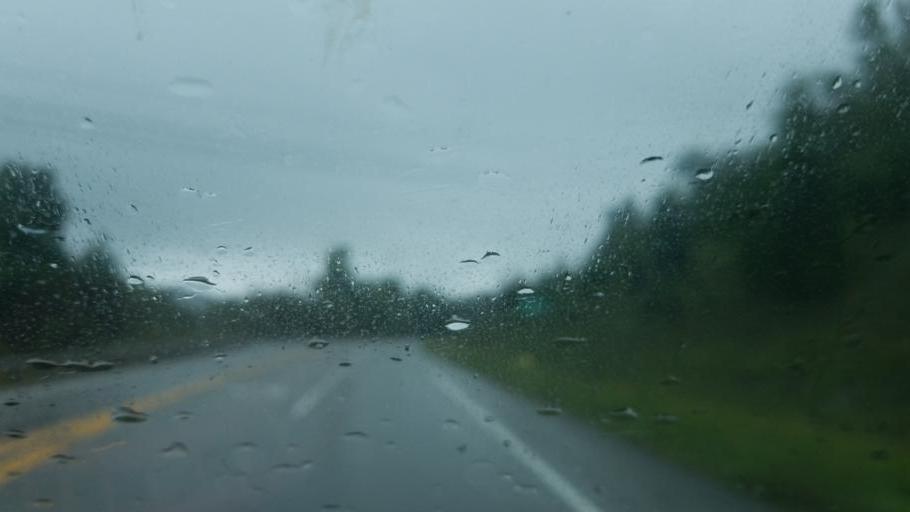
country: US
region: Kentucky
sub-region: Fleming County
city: Flemingsburg
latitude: 38.3645
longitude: -83.6168
